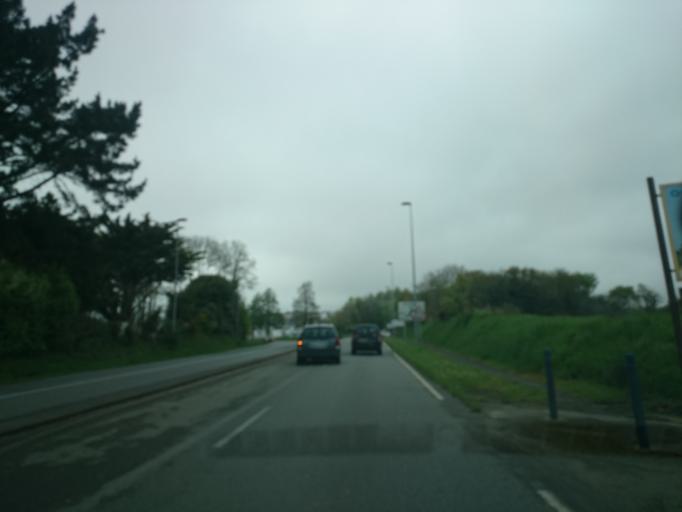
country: FR
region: Brittany
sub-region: Departement du Finistere
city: Gouesnou
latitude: 48.4449
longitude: -4.4638
